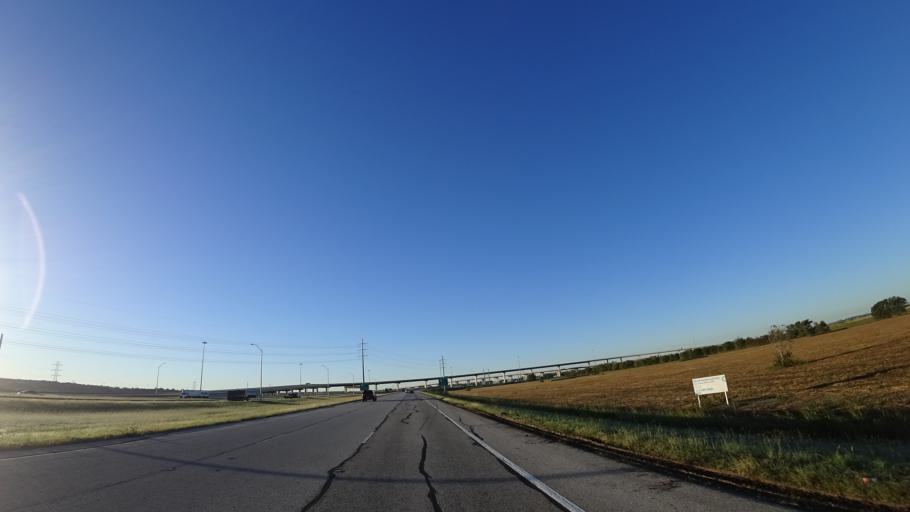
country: US
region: Texas
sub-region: Travis County
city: Hornsby Bend
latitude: 30.2028
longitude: -97.6233
